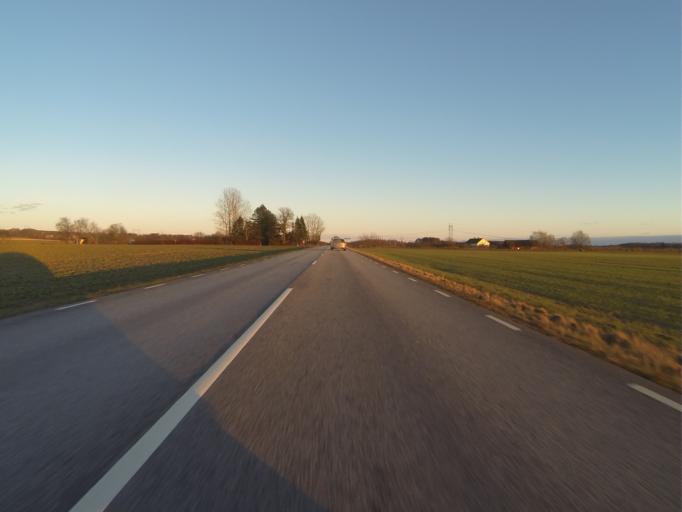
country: SE
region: Skane
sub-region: Hoors Kommun
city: Loberod
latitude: 55.7448
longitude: 13.4091
